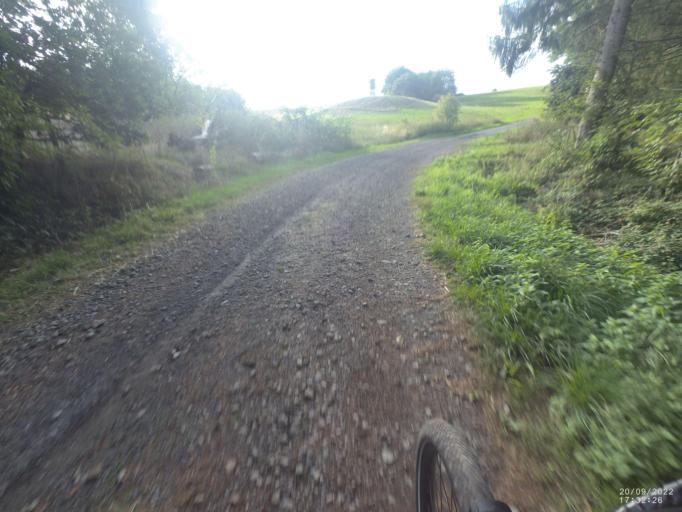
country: DE
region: Rheinland-Pfalz
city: Ellscheid
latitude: 50.1477
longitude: 6.9363
